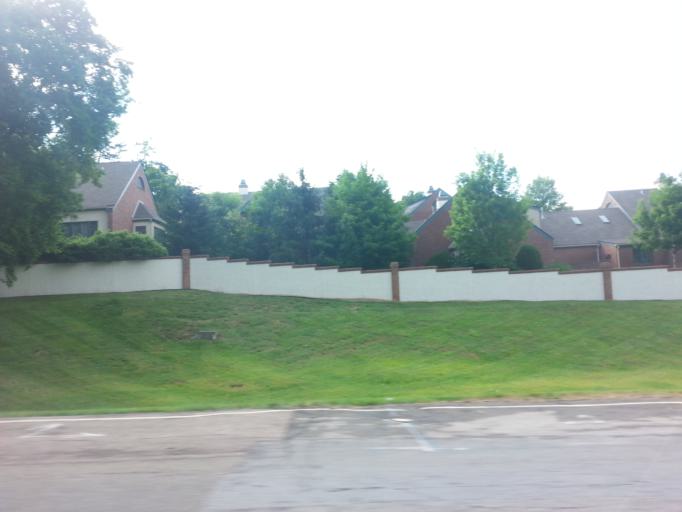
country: US
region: Tennessee
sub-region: Knox County
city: Knoxville
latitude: 35.9150
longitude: -83.9979
